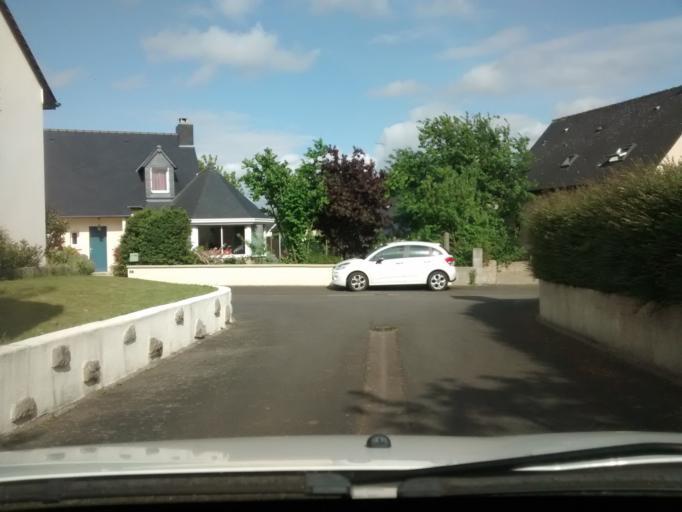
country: FR
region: Brittany
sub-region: Departement d'Ille-et-Vilaine
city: Vern-sur-Seiche
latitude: 48.0395
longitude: -1.6000
